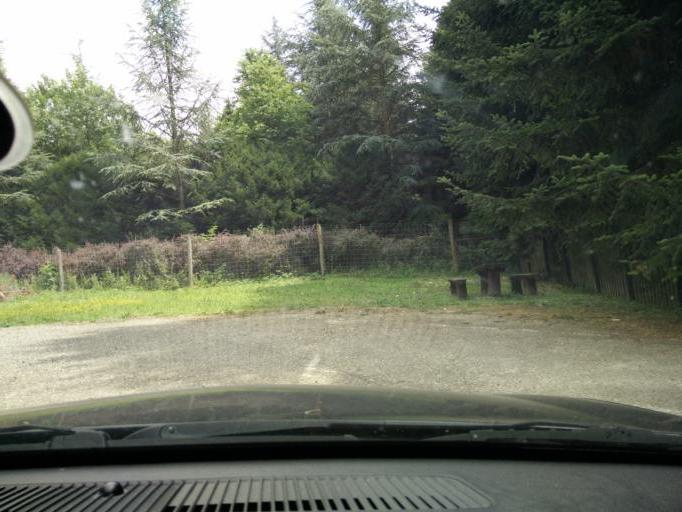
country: HU
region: Komarom-Esztergom
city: Tardos
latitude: 47.6590
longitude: 18.4179
